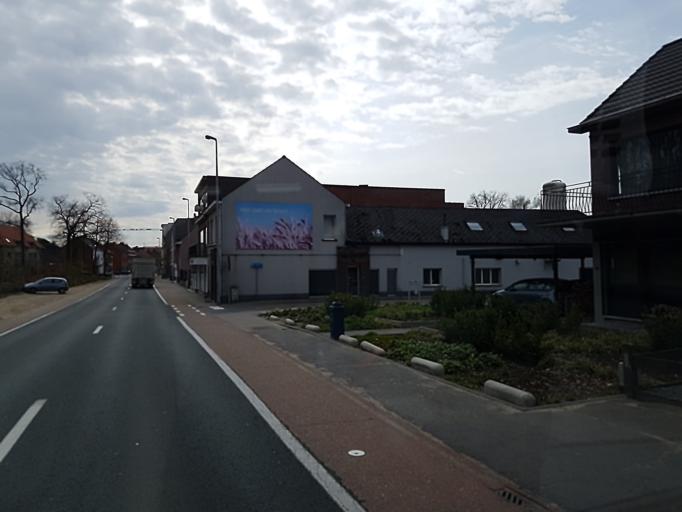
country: BE
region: Flanders
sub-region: Provincie Vlaams-Brabant
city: Scherpenheuvel-Zichem
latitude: 51.0297
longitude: 4.9791
